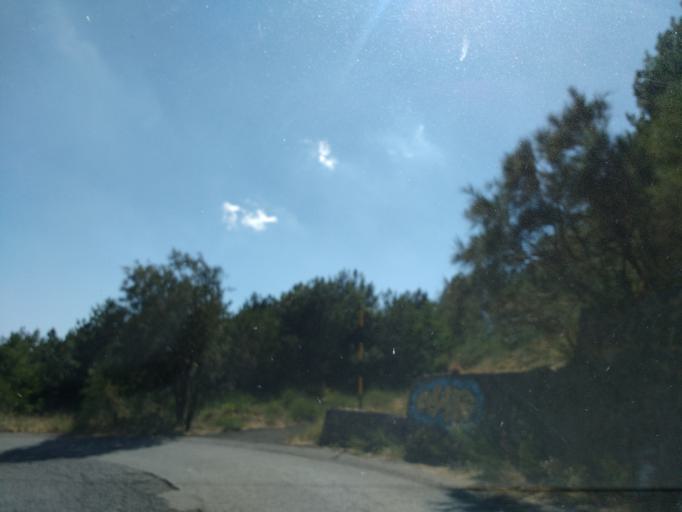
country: IT
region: Sicily
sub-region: Catania
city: Nicolosi
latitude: 37.6981
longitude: 15.0192
